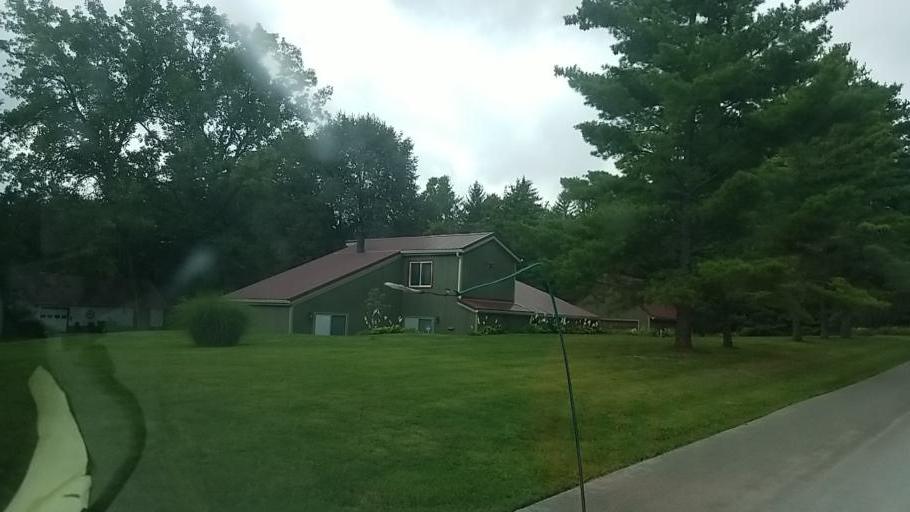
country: US
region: Ohio
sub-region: Pickaway County
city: Commercial Point
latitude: 39.8270
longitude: -83.0574
